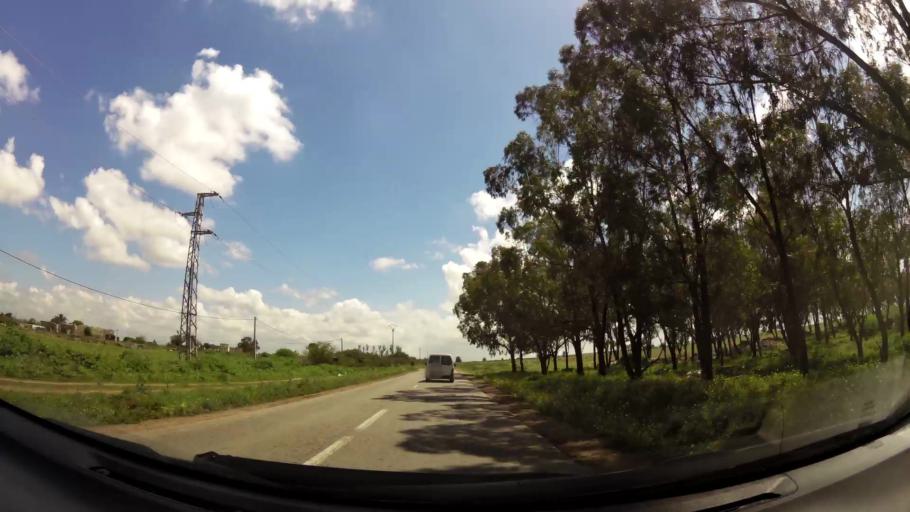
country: MA
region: Grand Casablanca
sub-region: Nouaceur
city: Dar Bouazza
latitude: 33.4156
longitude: -7.8097
